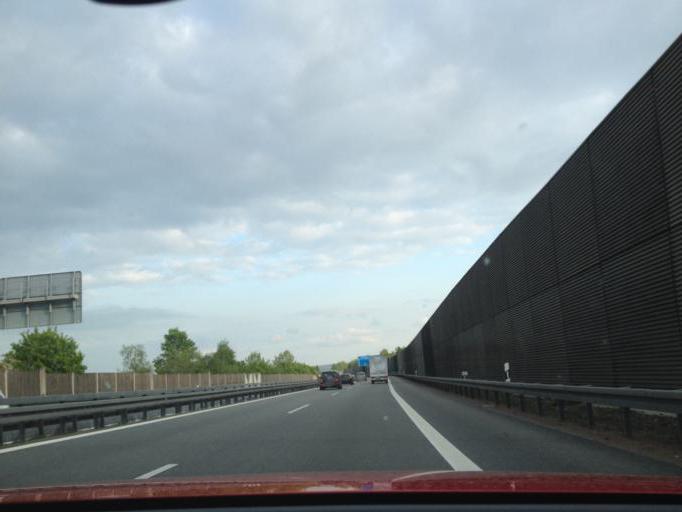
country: DE
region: Bavaria
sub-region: Upper Palatinate
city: Weiden
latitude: 49.6615
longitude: 12.1432
